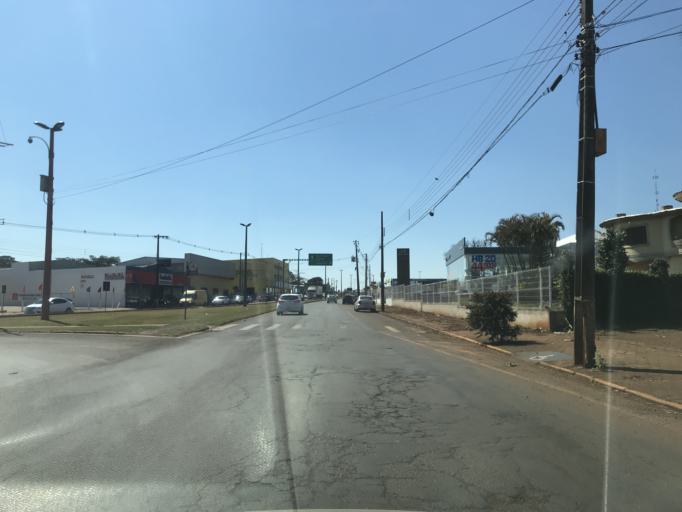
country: BR
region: Parana
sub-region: Toledo
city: Toledo
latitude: -24.7203
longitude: -53.7159
